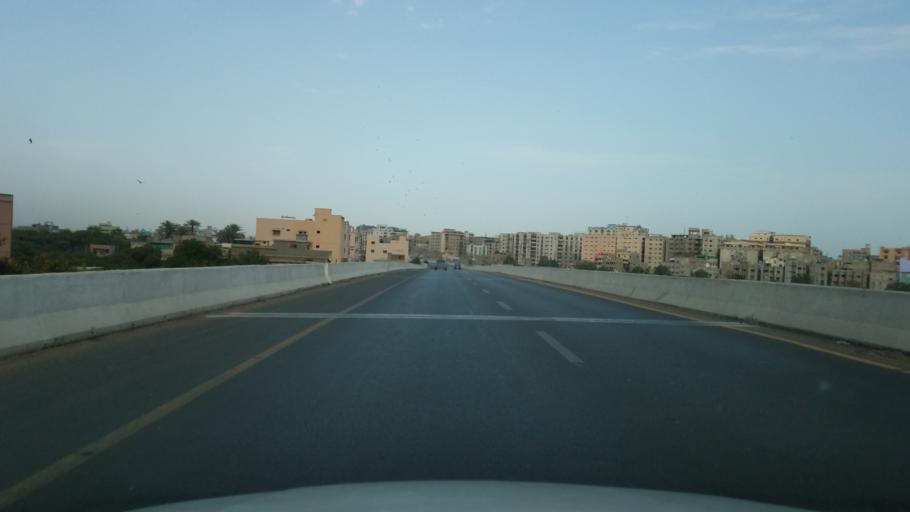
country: PK
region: Sindh
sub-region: Karachi District
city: Karachi
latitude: 24.8795
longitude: 67.0124
